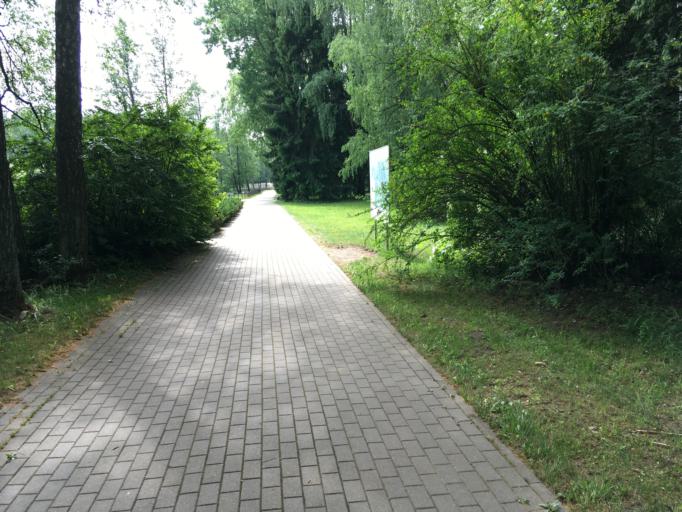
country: BY
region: Minsk
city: Minsk
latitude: 53.9135
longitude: 27.6146
